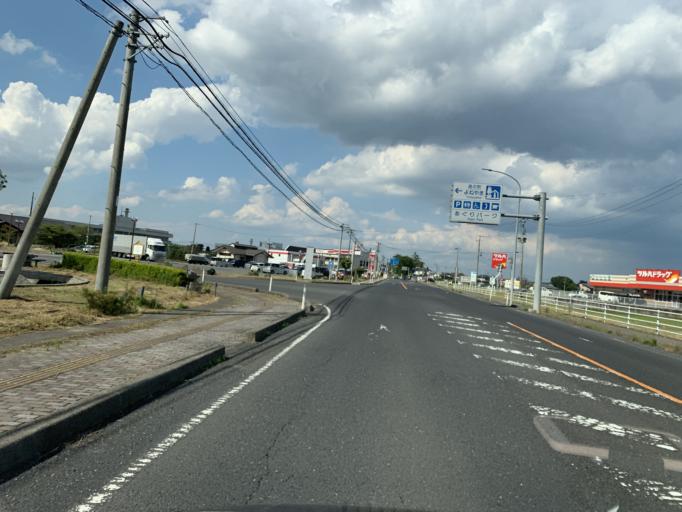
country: JP
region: Miyagi
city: Wakuya
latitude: 38.6266
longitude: 141.1887
